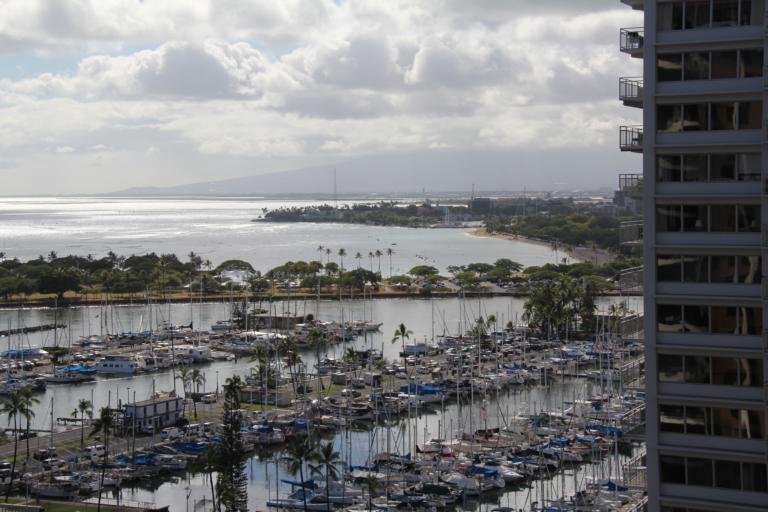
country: US
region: Hawaii
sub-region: Honolulu County
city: Honolulu
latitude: 21.2831
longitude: -157.8385
